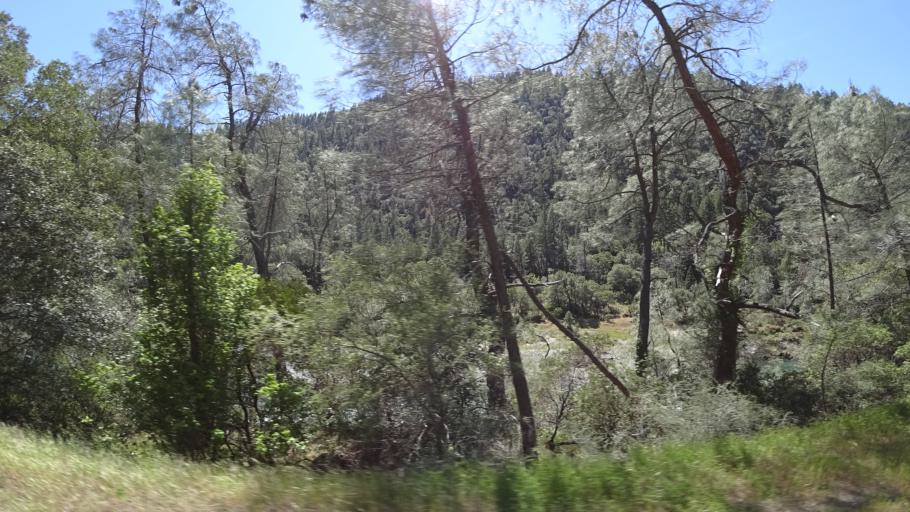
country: US
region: California
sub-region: Humboldt County
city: Willow Creek
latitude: 40.7879
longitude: -123.4294
